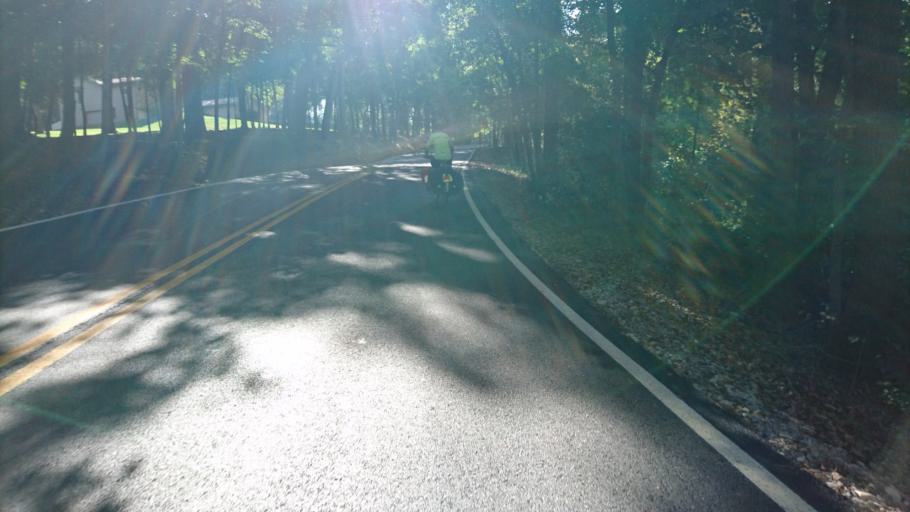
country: US
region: Missouri
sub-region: Saint Louis County
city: Eureka
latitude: 38.5409
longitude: -90.6329
